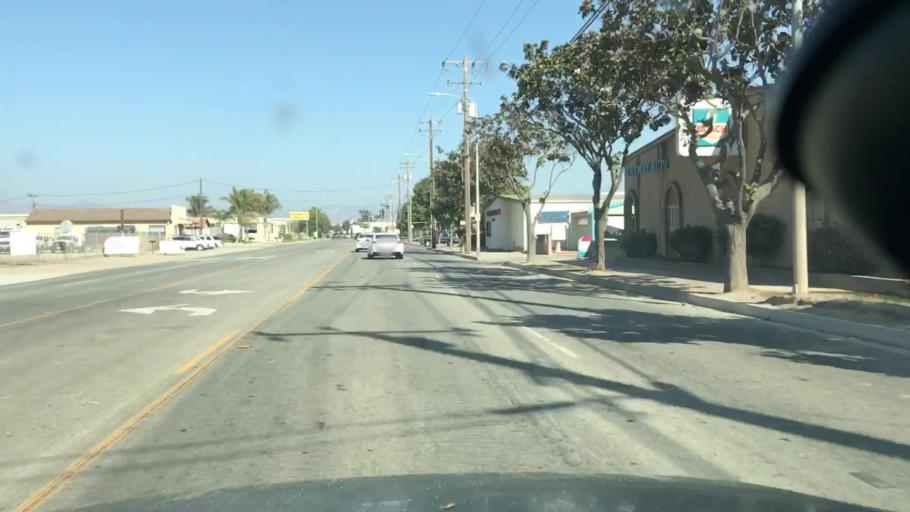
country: US
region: California
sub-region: Santa Barbara County
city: Santa Maria
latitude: 34.9204
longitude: -120.4447
